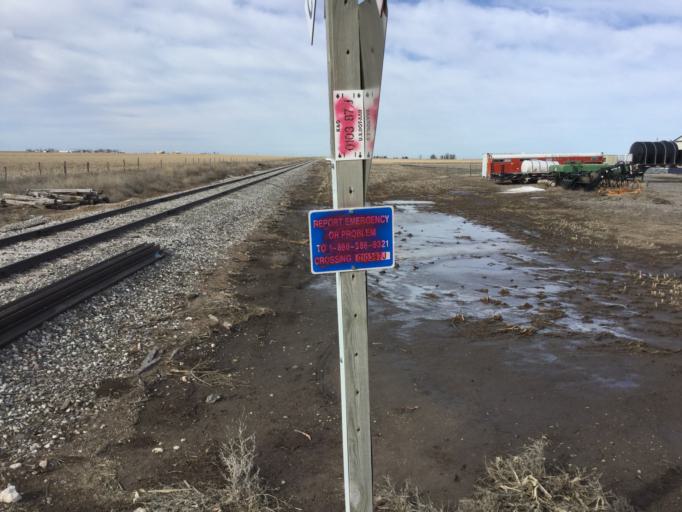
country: US
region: Kansas
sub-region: Lane County
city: Dighton
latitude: 38.4863
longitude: -100.4762
